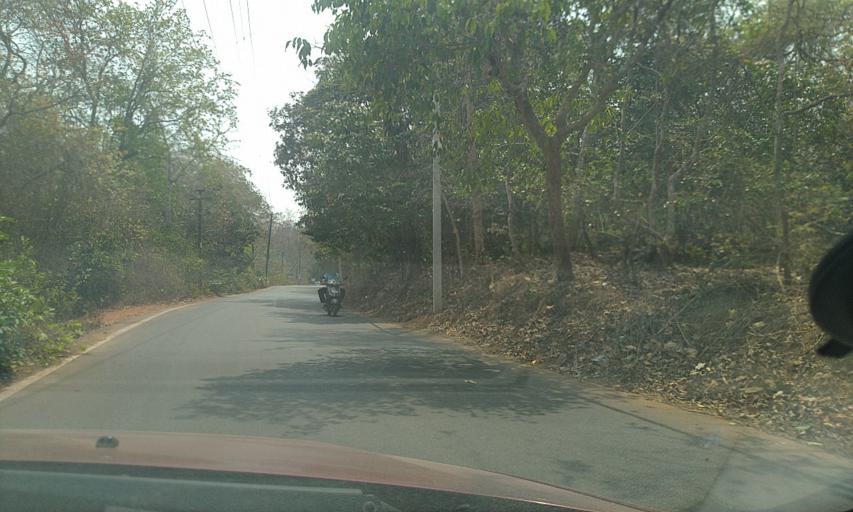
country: IN
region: Goa
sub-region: North Goa
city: Solim
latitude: 15.5977
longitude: 73.7820
